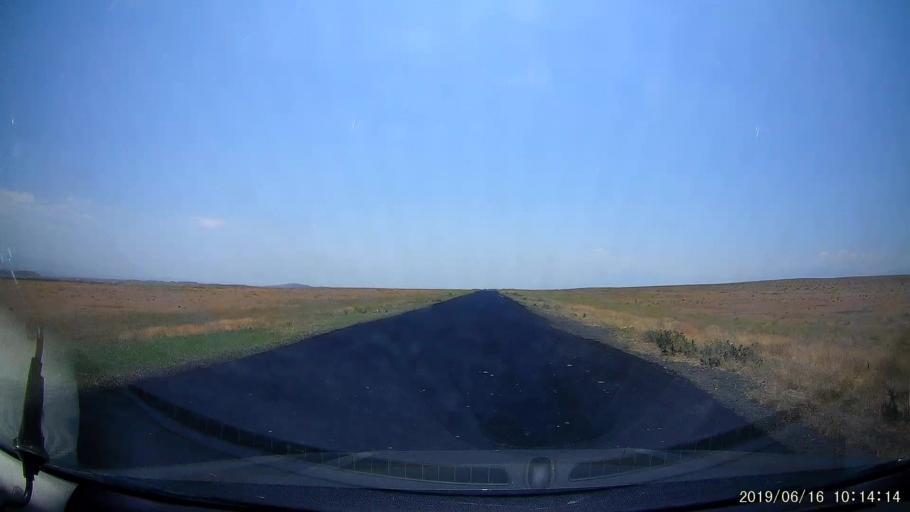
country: TR
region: Igdir
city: Tuzluca
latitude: 40.1866
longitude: 43.6585
